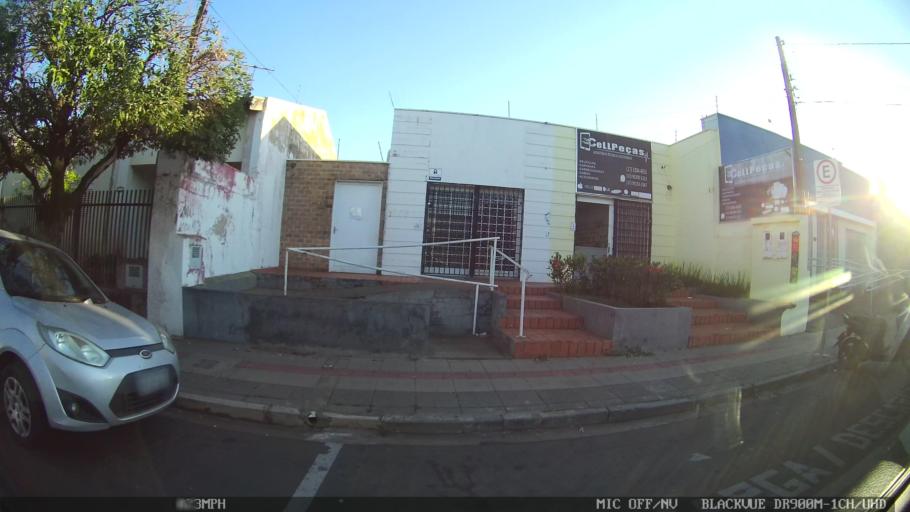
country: BR
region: Sao Paulo
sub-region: Sao Jose Do Rio Preto
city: Sao Jose do Rio Preto
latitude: -20.8010
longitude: -49.3863
